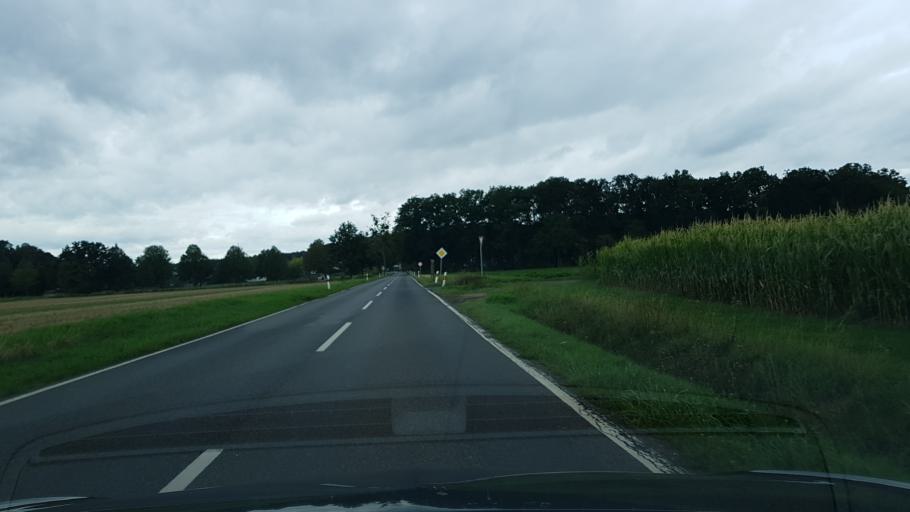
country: DE
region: North Rhine-Westphalia
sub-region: Regierungsbezirk Koln
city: Wachtberg
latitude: 50.6134
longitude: 7.0717
